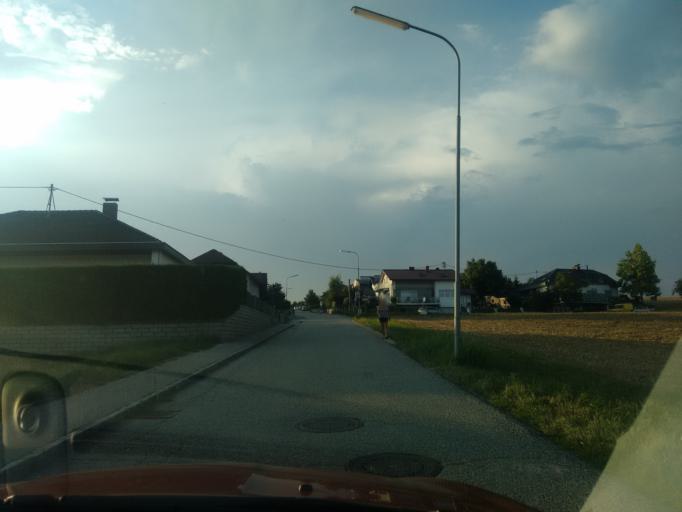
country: AT
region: Upper Austria
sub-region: Politischer Bezirk Grieskirchen
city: Bad Schallerbach
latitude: 48.1876
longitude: 13.8976
